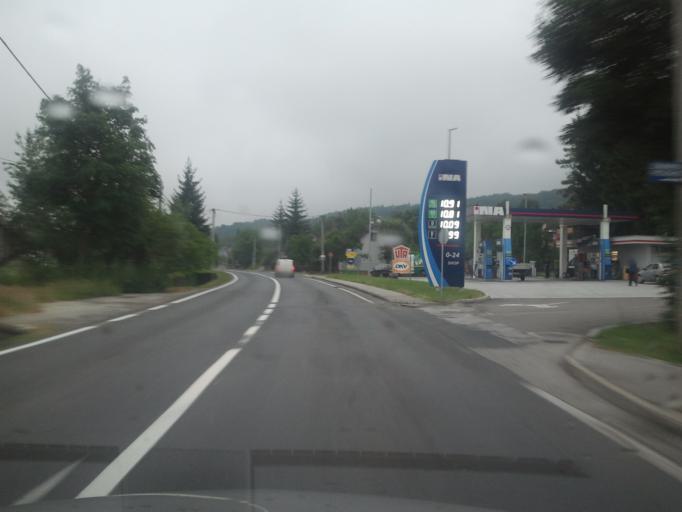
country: HR
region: Karlovacka
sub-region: Grad Karlovac
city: Slunj
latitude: 45.1085
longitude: 15.5855
